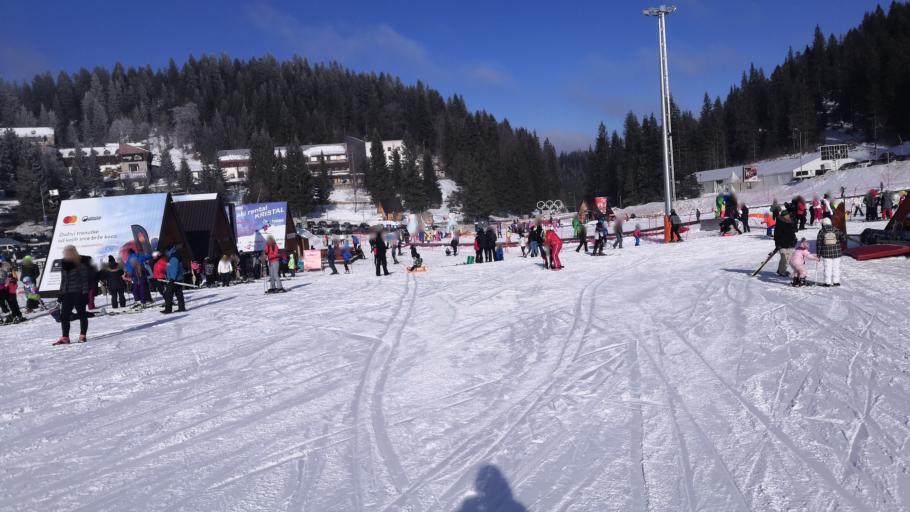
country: BA
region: Republika Srpska
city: Koran
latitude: 43.7360
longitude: 18.5665
